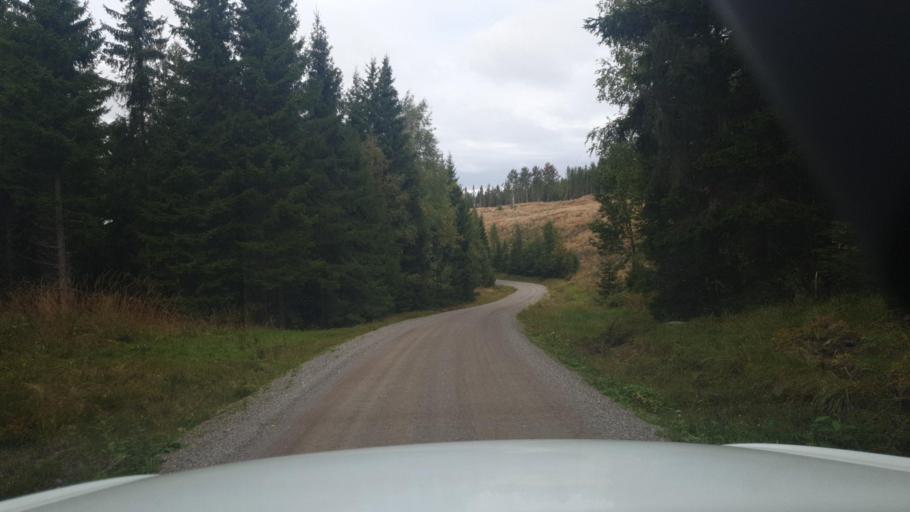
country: SE
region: Vaermland
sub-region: Eda Kommun
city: Charlottenberg
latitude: 60.0391
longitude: 12.6296
